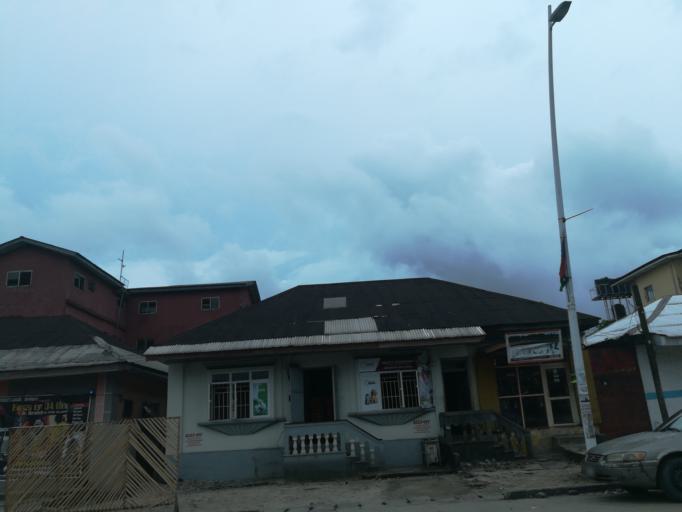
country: NG
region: Rivers
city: Port Harcourt
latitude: 4.7621
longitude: 7.0302
